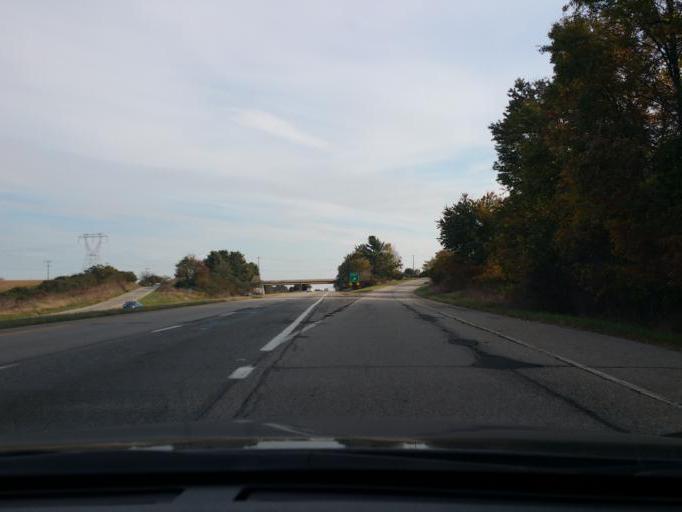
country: US
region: Pennsylvania
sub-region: Chester County
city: Oxford
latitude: 39.7851
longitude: -75.9986
